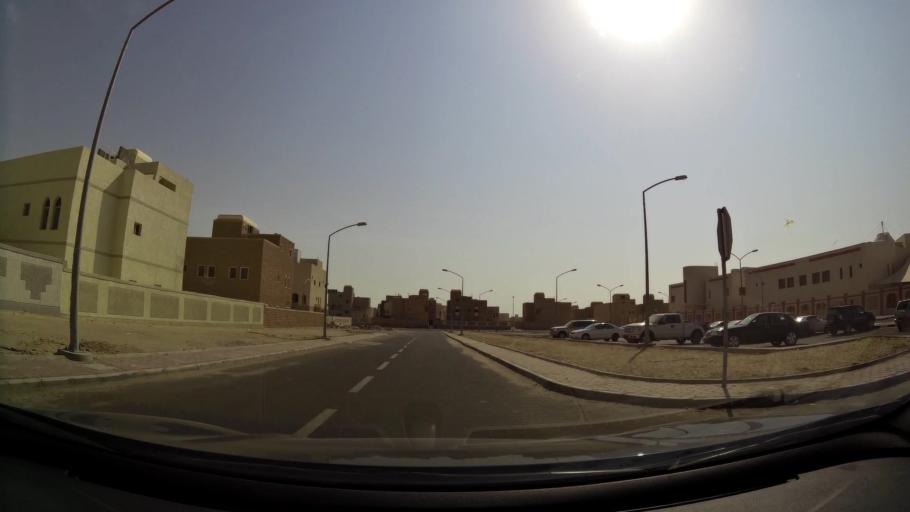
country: KW
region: Al Ahmadi
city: Al Wafrah
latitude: 28.7998
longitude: 48.0724
